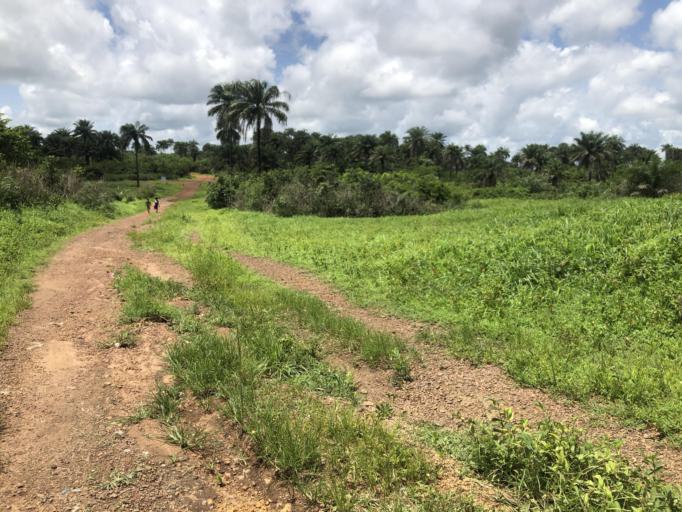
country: SL
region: Northern Province
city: Port Loko
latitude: 8.7172
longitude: -12.8470
